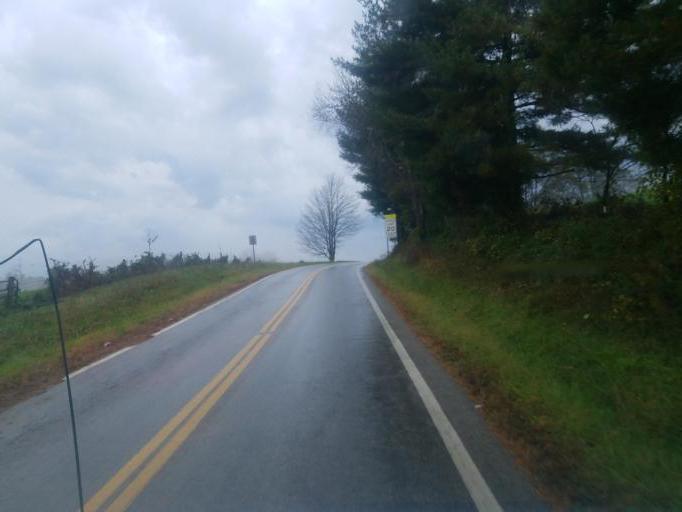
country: US
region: Ohio
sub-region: Morgan County
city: McConnelsville
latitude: 39.4929
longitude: -81.8877
